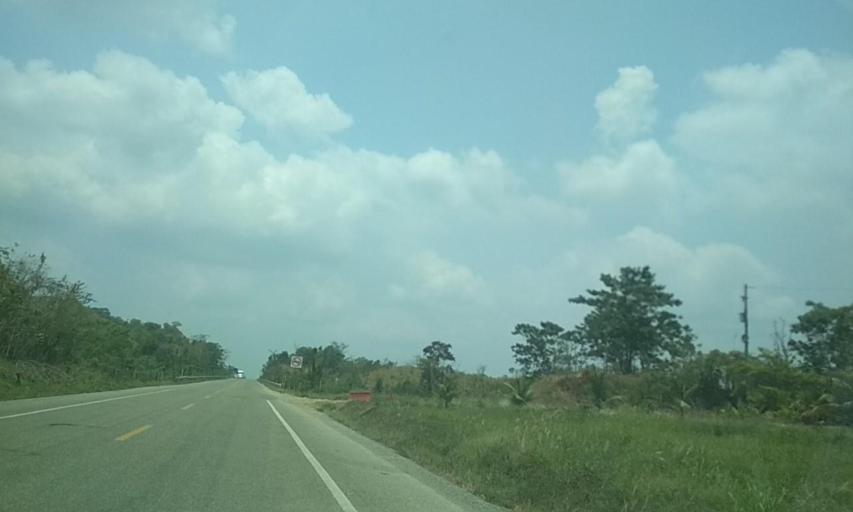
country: MX
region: Tabasco
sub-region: Huimanguillo
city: Francisco Rueda
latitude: 17.6443
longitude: -93.8252
